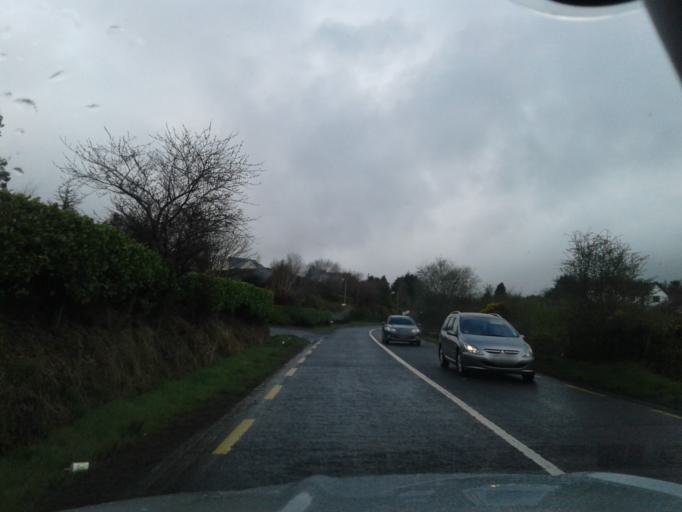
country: IE
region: Ulster
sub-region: County Donegal
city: Letterkenny
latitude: 54.9700
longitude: -7.6896
